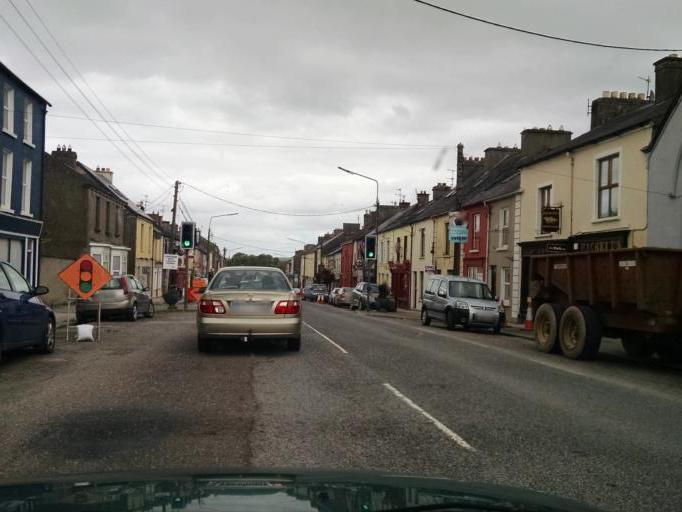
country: IE
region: Munster
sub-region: County Cork
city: Mallow
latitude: 52.2318
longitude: -8.6701
